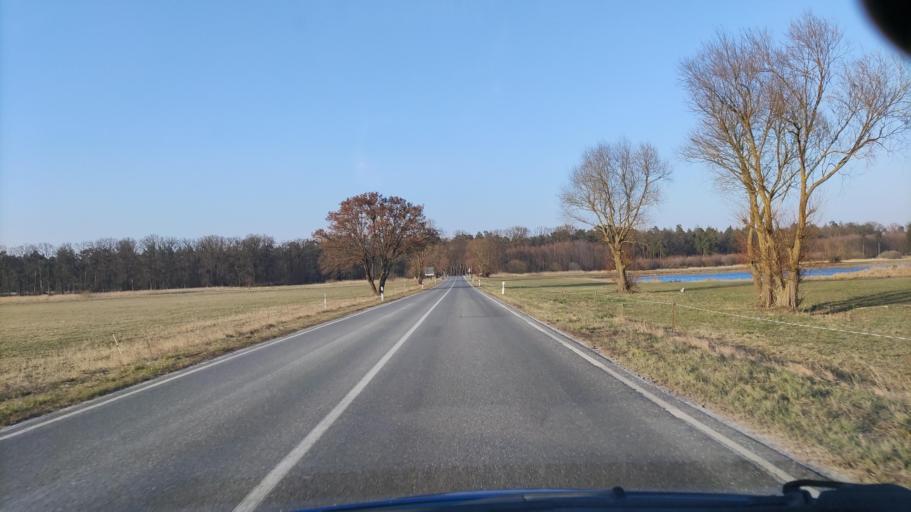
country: DE
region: Brandenburg
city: Lanz
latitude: 52.9961
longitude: 11.5494
